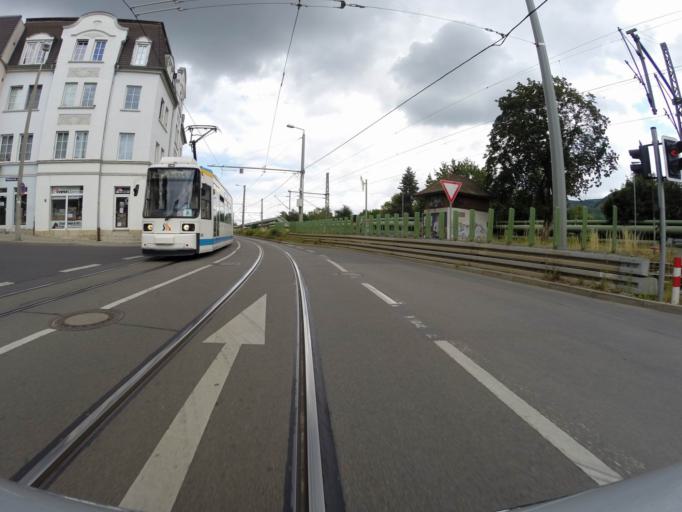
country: DE
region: Thuringia
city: Jena
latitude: 50.9159
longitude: 11.5780
